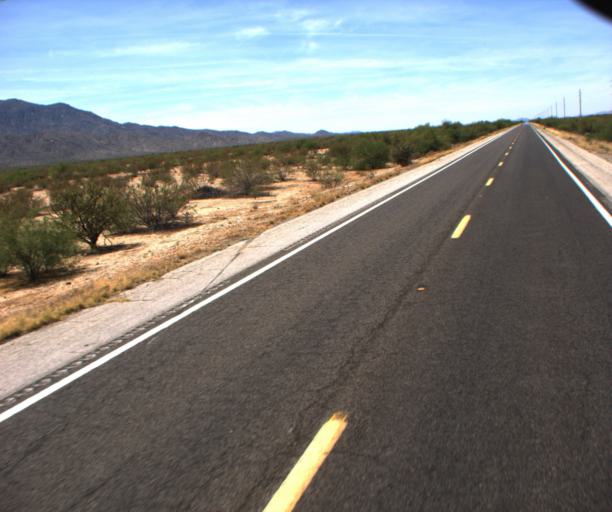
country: US
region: Arizona
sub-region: La Paz County
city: Salome
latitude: 33.8986
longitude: -113.3113
